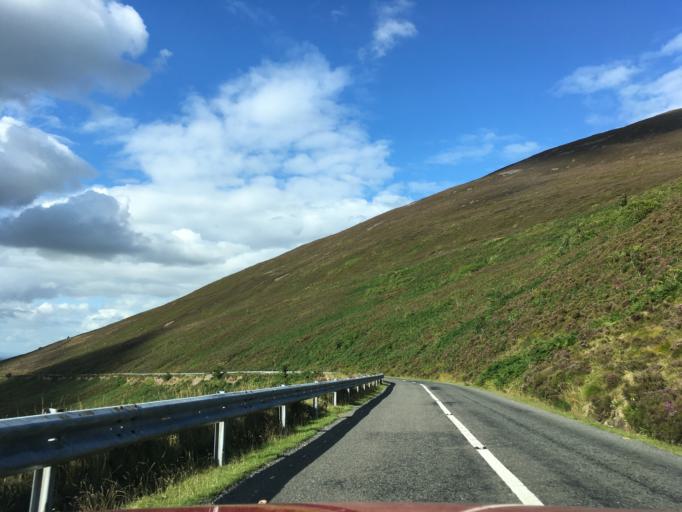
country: IE
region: Munster
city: Cahir
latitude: 52.2432
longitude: -7.9550
